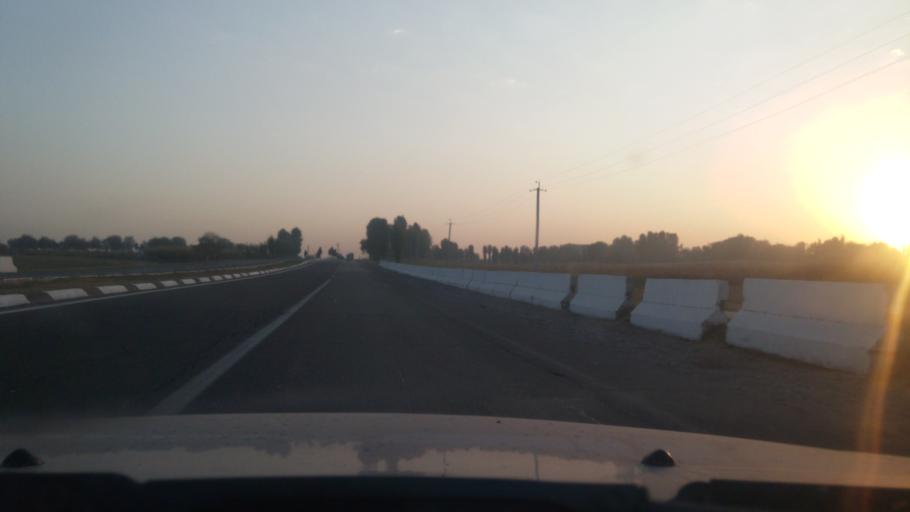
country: UZ
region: Toshkent
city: Amir Timur
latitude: 41.0963
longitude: 68.9608
